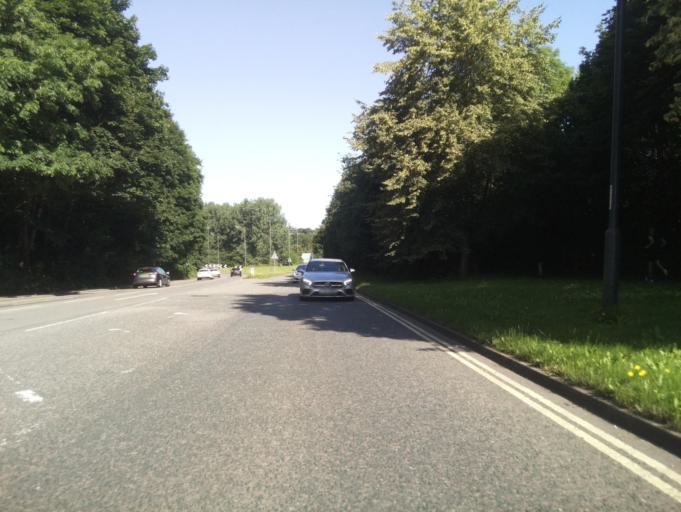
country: GB
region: England
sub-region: Derby
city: Derby
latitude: 52.9202
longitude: -1.5105
